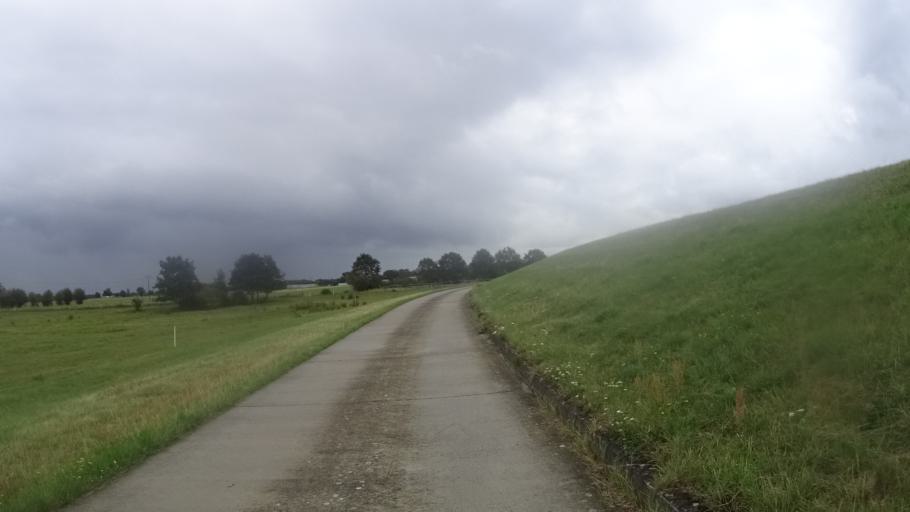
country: DE
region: Lower Saxony
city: Neu Darchau
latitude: 53.2553
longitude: 10.8626
